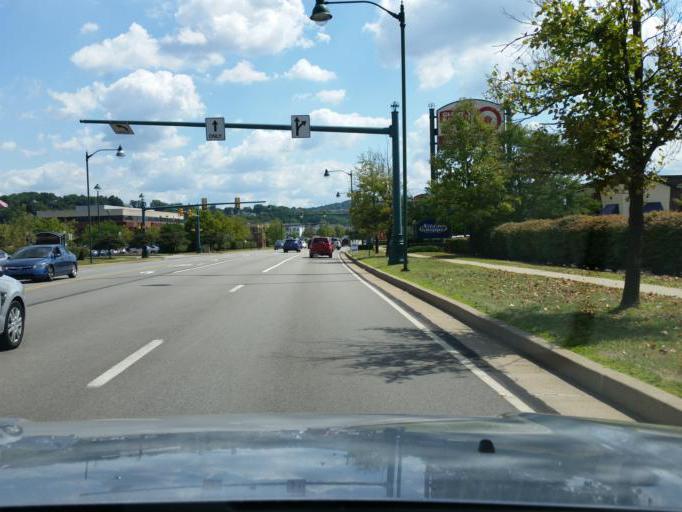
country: US
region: Pennsylvania
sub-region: Allegheny County
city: Homestead
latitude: 40.4119
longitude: -79.9117
